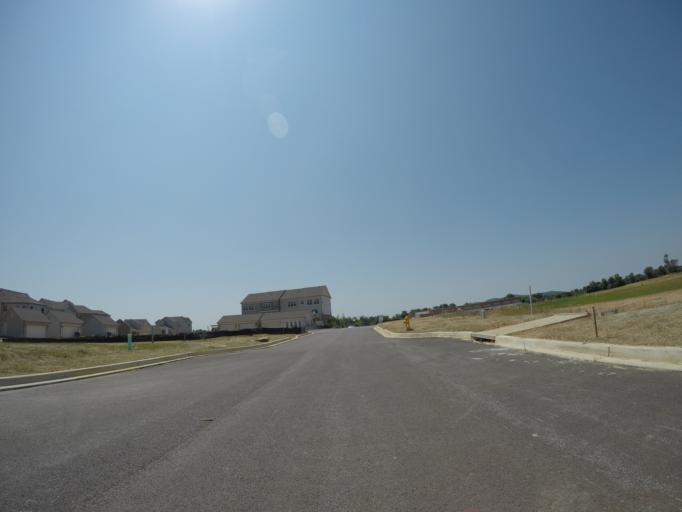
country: US
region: Maryland
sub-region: Frederick County
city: Urbana
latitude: 39.3298
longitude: -77.3649
